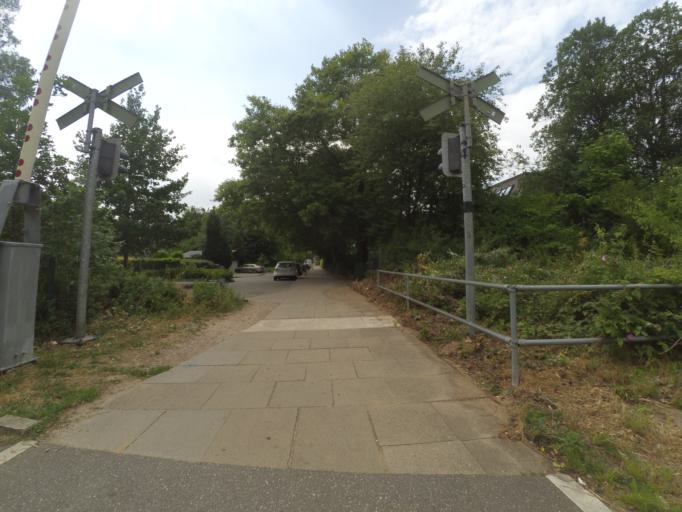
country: DE
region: Hamburg
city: Eidelstedt
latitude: 53.6229
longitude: 9.9057
